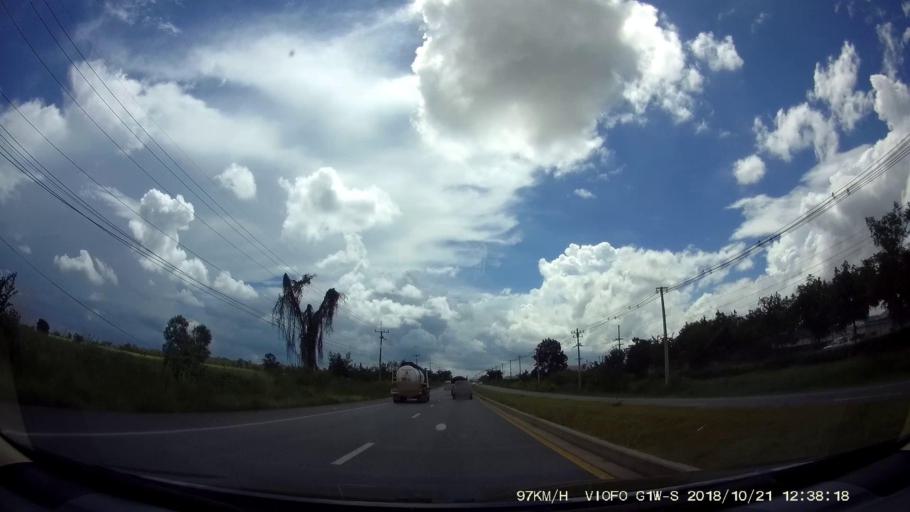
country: TH
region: Nakhon Ratchasima
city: Amphoe Sikhiu
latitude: 15.0561
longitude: 101.7068
